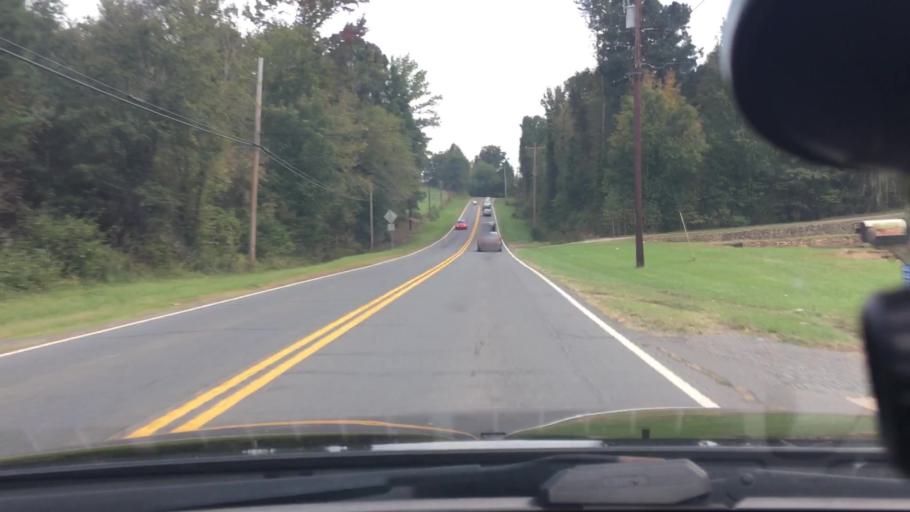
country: US
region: North Carolina
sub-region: Stanly County
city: Albemarle
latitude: 35.3403
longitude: -80.1388
